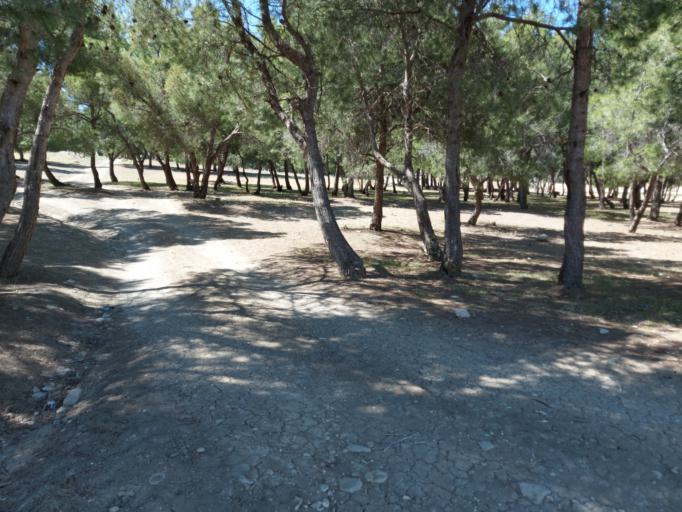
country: TN
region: Kef
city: El Kef
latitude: 36.1847
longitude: 8.7301
